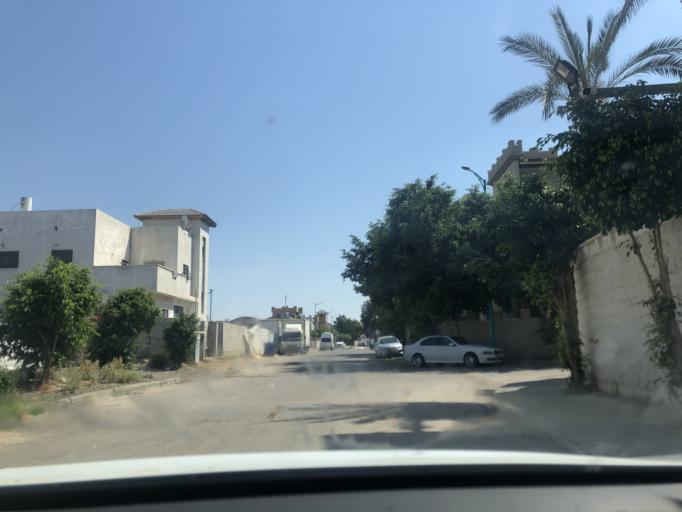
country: IL
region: Central District
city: Lod
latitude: 31.9536
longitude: 34.8768
